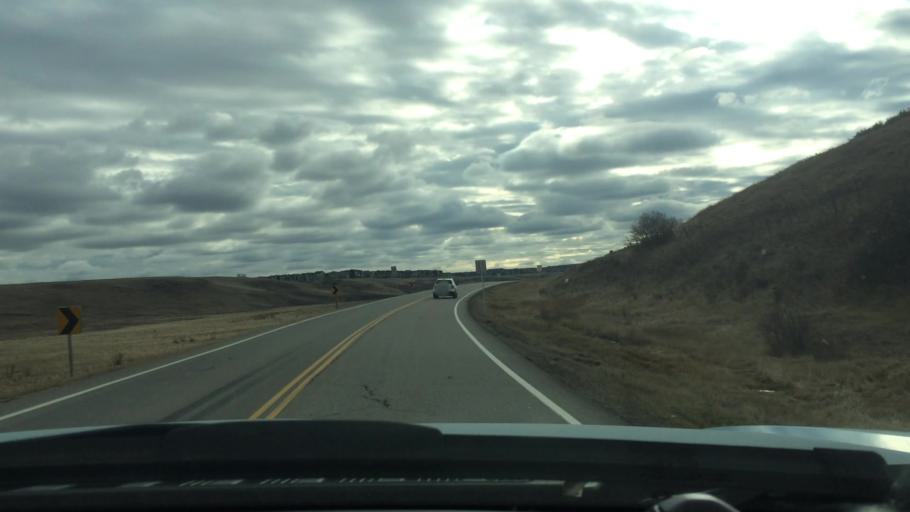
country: CA
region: Alberta
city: Calgary
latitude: 51.1885
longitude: -114.1410
